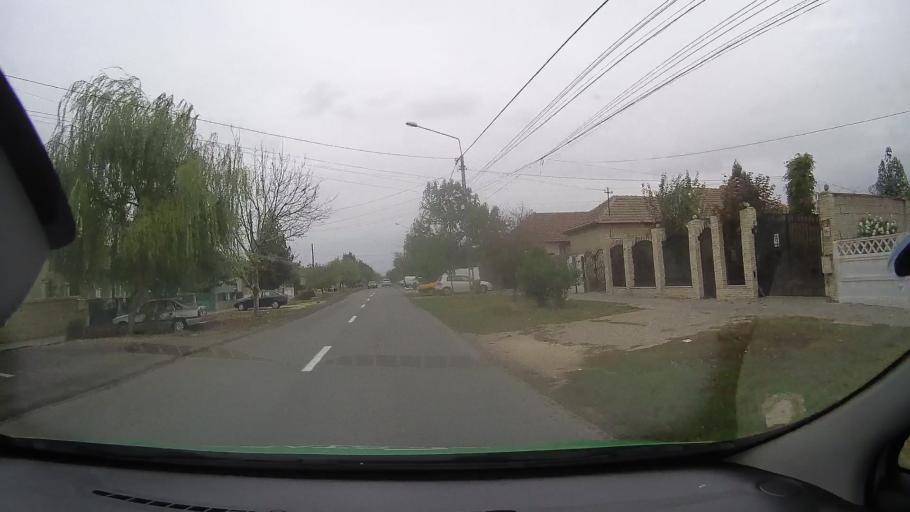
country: RO
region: Constanta
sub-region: Comuna Mihail Kogalniceanu
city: Mihail Kogalniceanu
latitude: 44.3710
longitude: 28.4635
